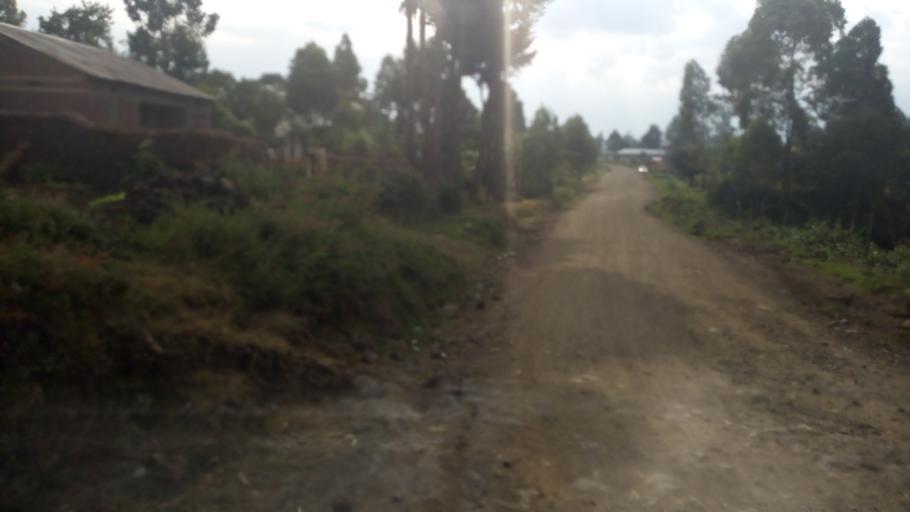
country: UG
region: Western Region
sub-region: Kisoro District
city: Kisoro
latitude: -1.2917
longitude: 29.6966
